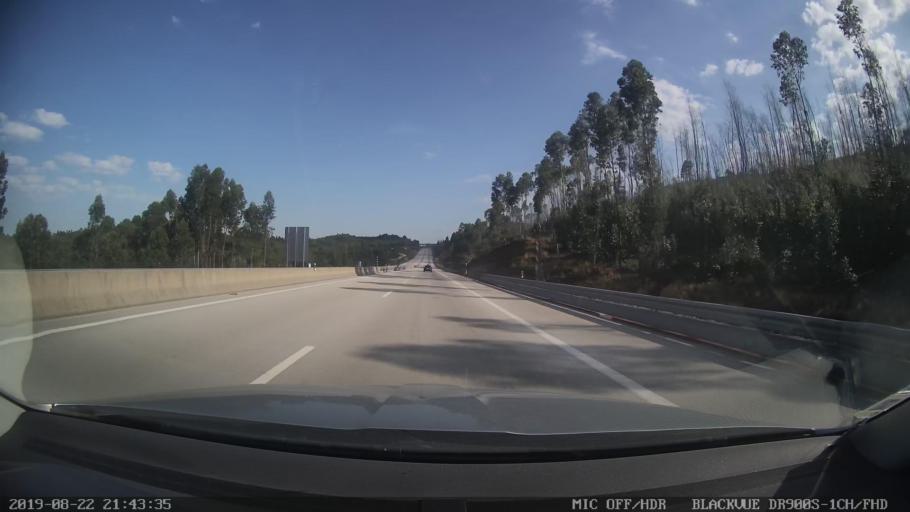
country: PT
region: Leiria
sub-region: Figueiro Dos Vinhos
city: Figueiro dos Vinhos
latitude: 39.9366
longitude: -8.3470
